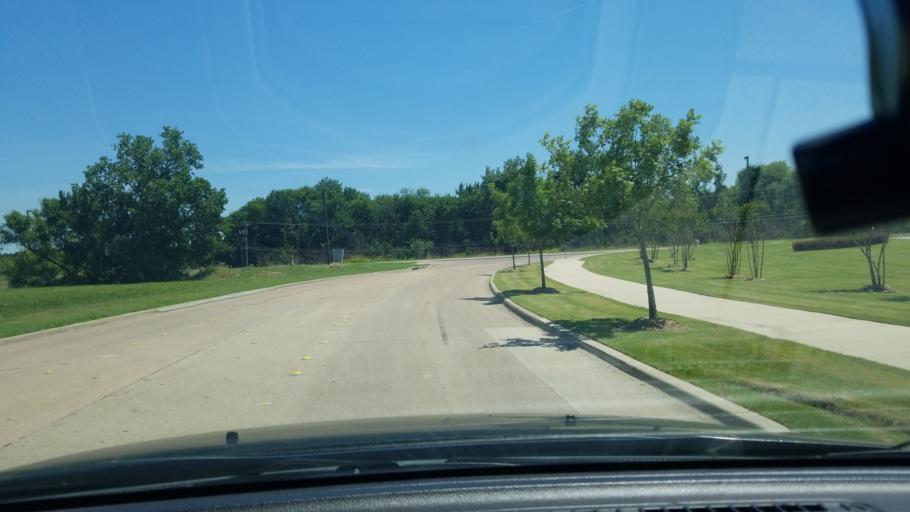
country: US
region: Texas
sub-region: Dallas County
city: Mesquite
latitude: 32.7684
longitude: -96.6193
